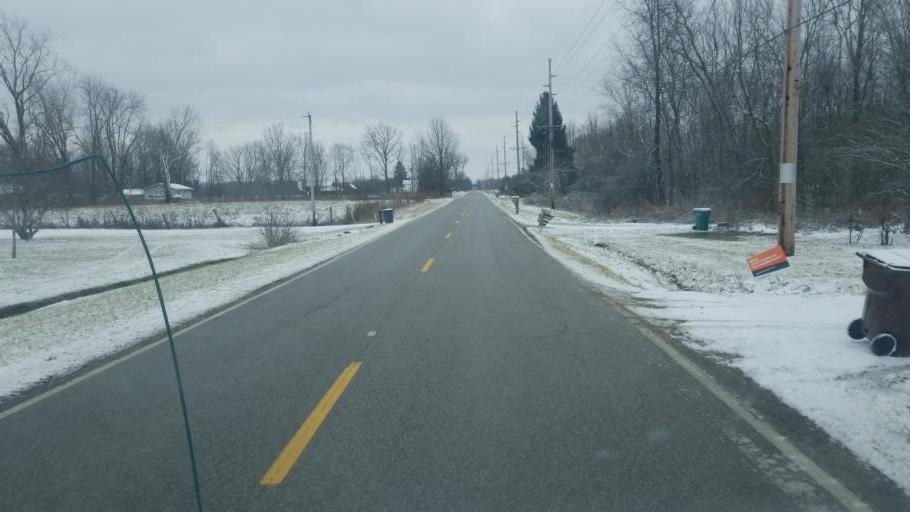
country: US
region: Ohio
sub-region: Delaware County
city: Sunbury
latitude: 40.2767
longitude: -82.7865
